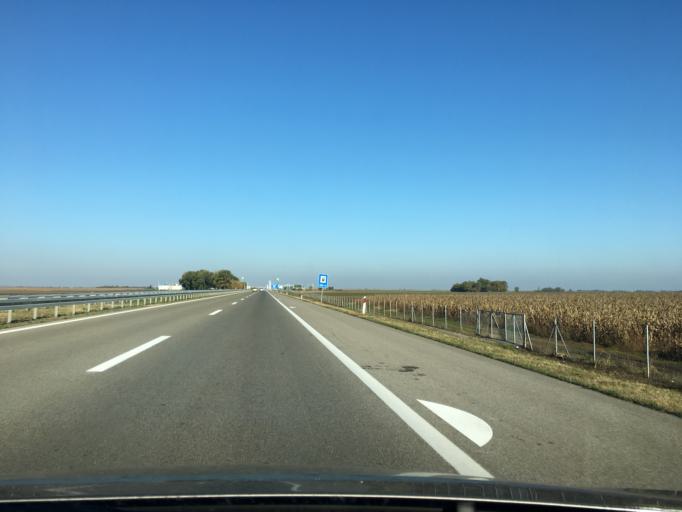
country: RS
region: Autonomna Pokrajina Vojvodina
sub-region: Severnobacki Okrug
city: Backa Topola
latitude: 45.7871
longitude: 19.6965
